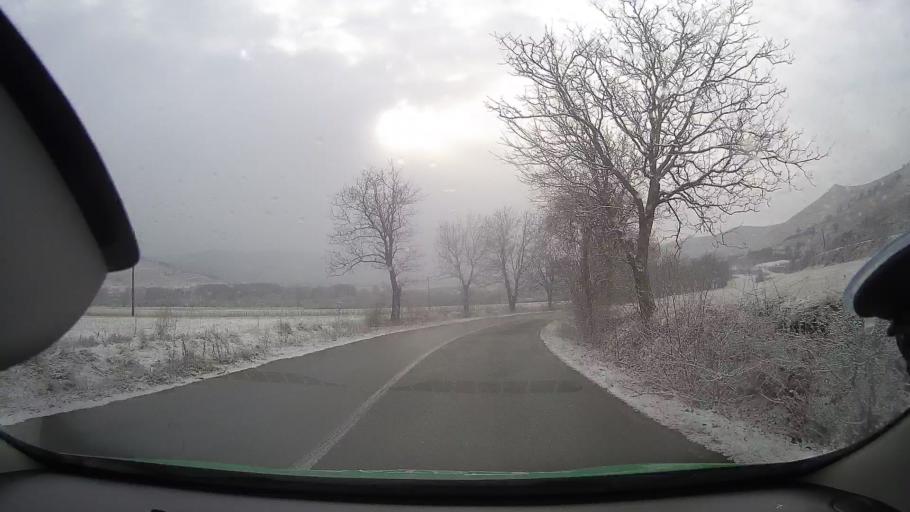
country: RO
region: Alba
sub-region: Comuna Rimetea
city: Rimetea
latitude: 46.4408
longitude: 23.5638
